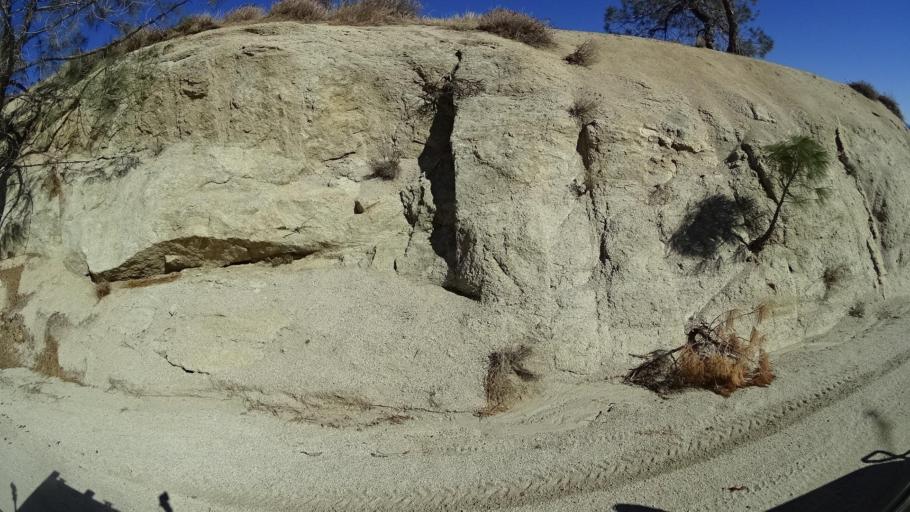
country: US
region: California
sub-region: Kern County
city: Wofford Heights
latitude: 35.6993
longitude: -118.4834
